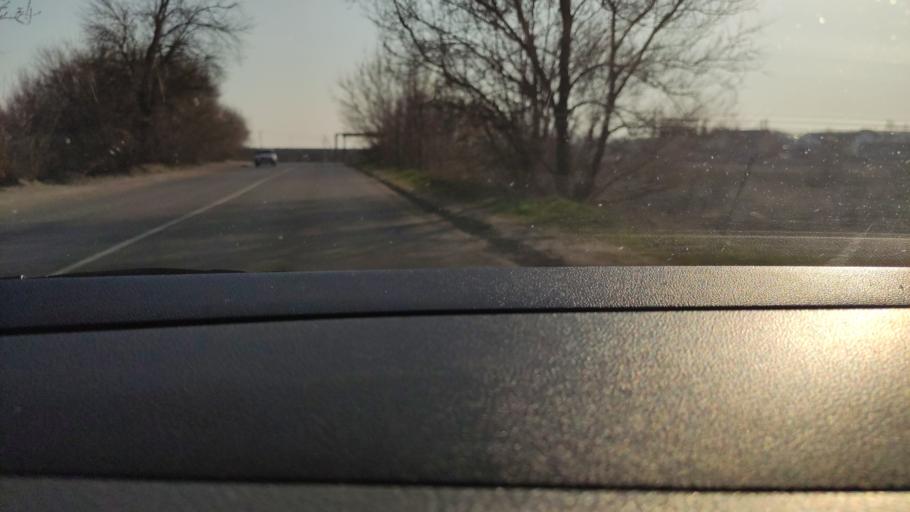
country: RU
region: Voronezj
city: Maslovka
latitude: 51.5788
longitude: 39.3138
